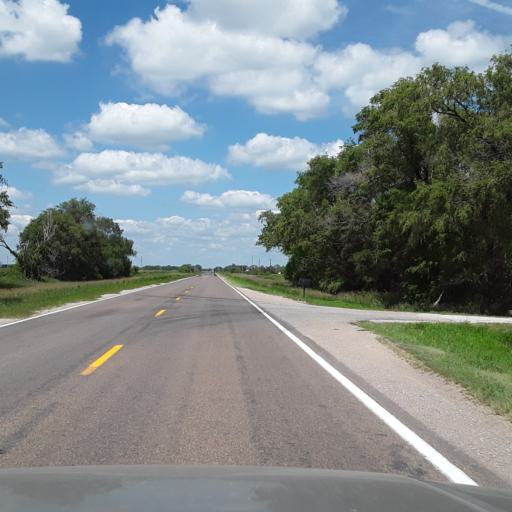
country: US
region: Nebraska
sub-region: Nance County
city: Genoa
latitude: 41.3760
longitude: -97.6944
